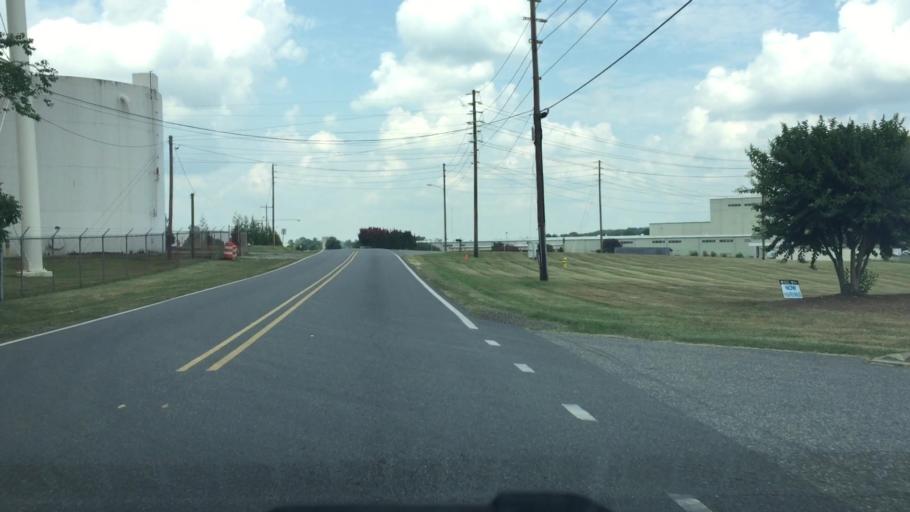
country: US
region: North Carolina
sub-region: Iredell County
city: Troutman
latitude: 35.7124
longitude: -80.8913
